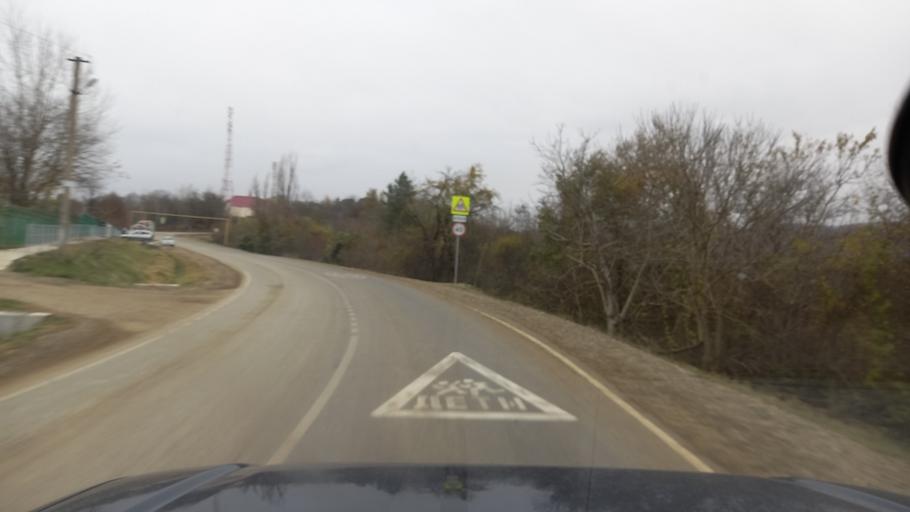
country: RU
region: Krasnodarskiy
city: Goryachiy Klyuch
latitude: 44.5160
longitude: 39.2946
